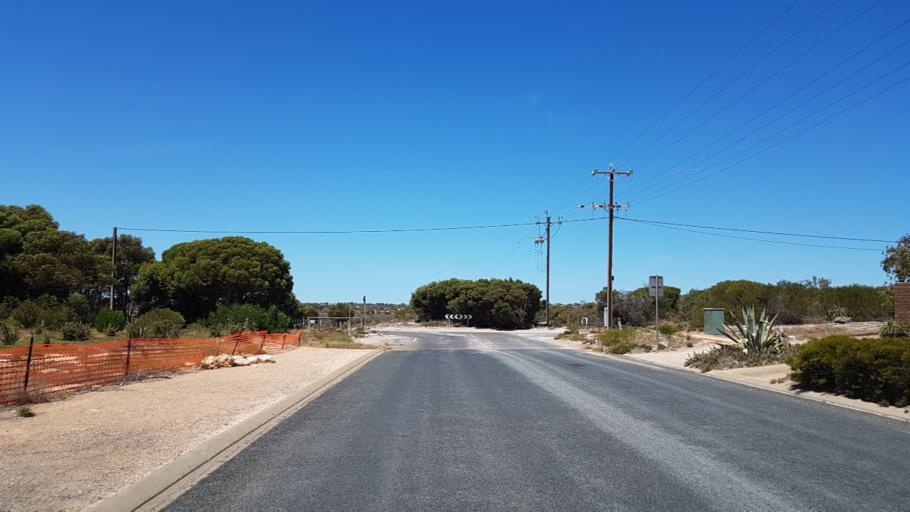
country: AU
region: South Australia
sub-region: Copper Coast
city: Wallaroo
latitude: -33.9063
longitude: 137.6331
